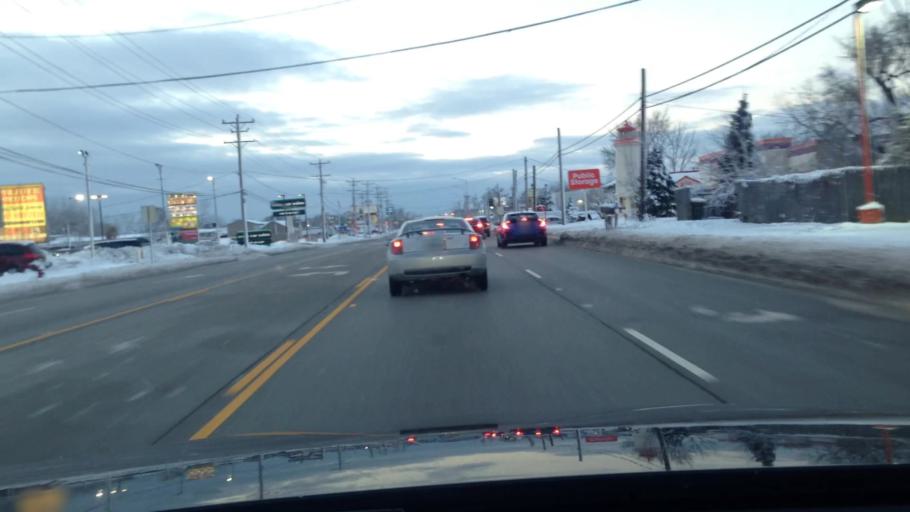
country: US
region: Illinois
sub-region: Lake County
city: Kildeer
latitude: 42.1505
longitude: -88.0346
